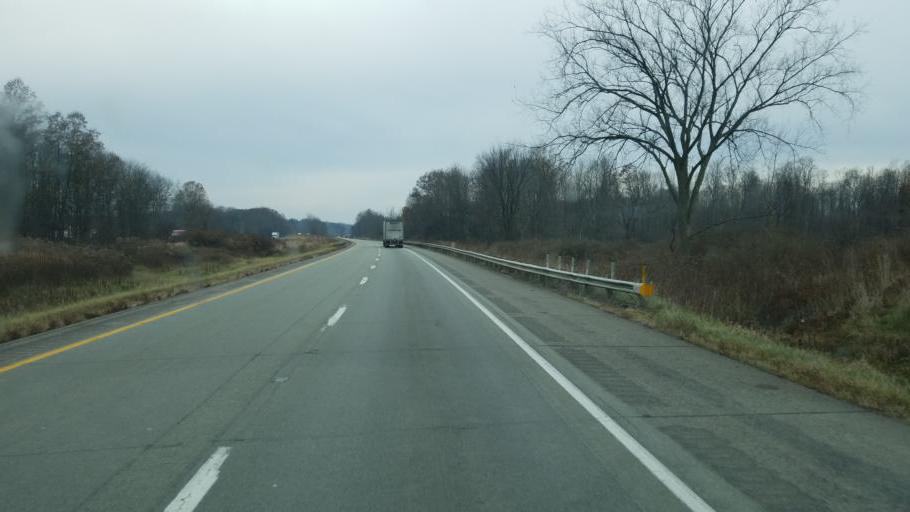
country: US
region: Pennsylvania
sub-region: Mercer County
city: Mercer
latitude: 41.1959
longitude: -80.1882
